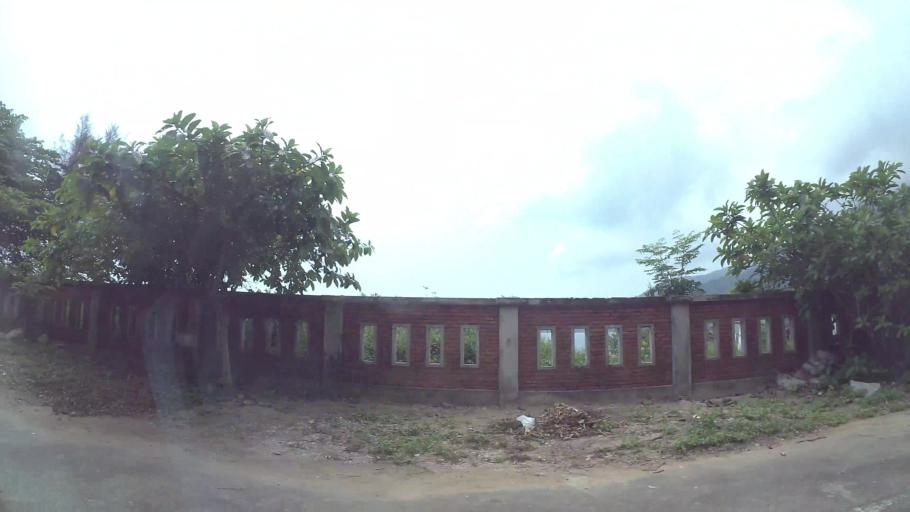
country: VN
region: Da Nang
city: Son Tra
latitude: 16.1041
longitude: 108.3007
